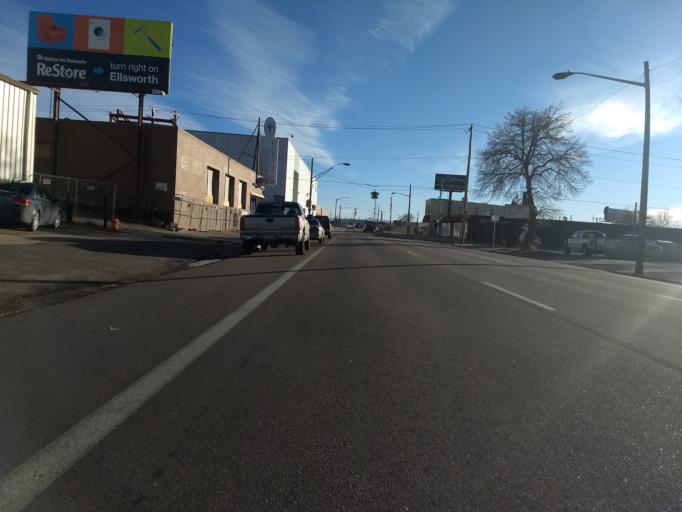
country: US
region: Colorado
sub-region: Denver County
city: Denver
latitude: 39.7173
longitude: -105.0002
